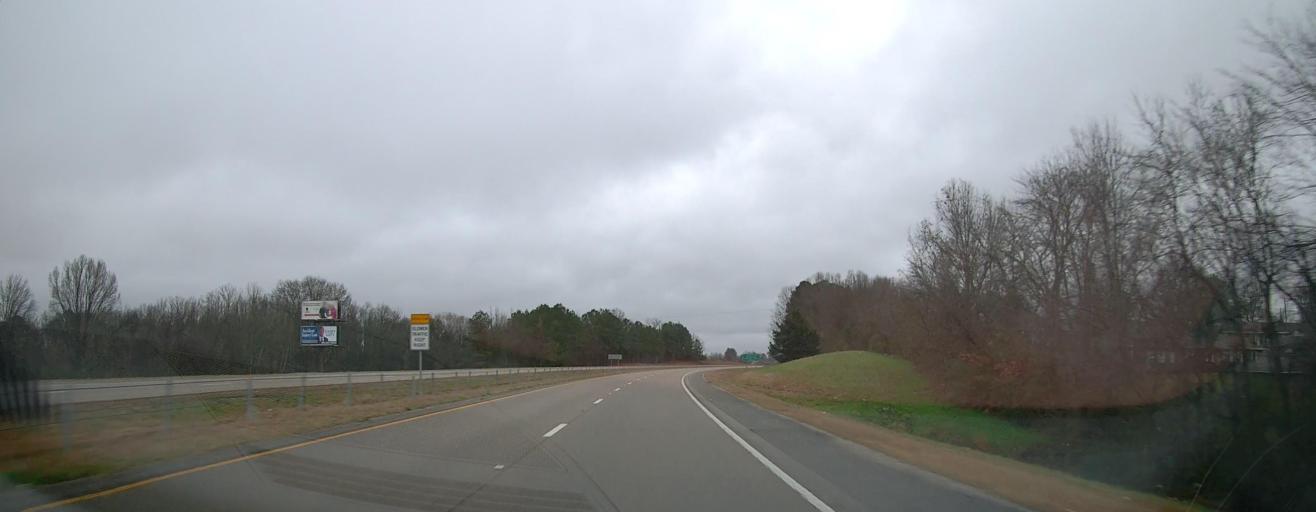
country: US
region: Mississippi
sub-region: Alcorn County
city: Corinth
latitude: 34.9194
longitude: -88.5423
